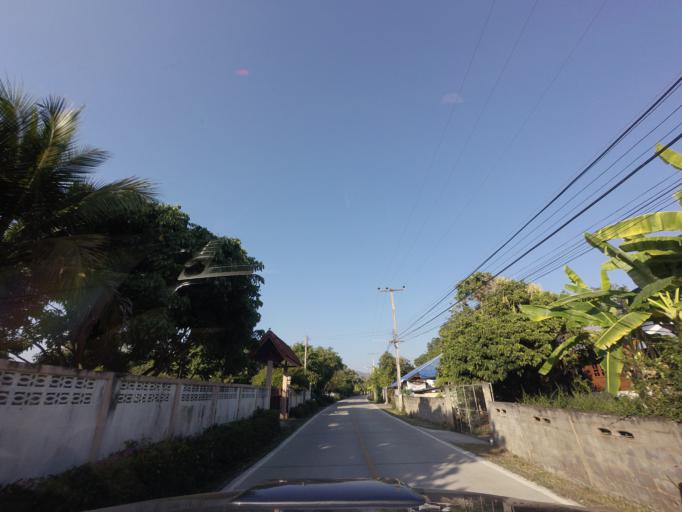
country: TH
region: Chiang Mai
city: San Sai
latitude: 18.9033
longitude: 99.1308
